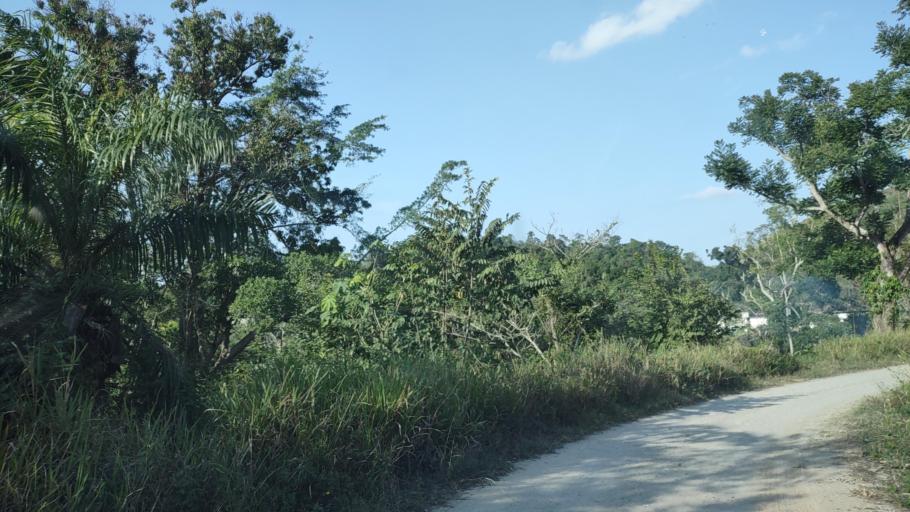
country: MX
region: Veracruz
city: Papantla de Olarte
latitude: 20.4589
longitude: -97.3622
